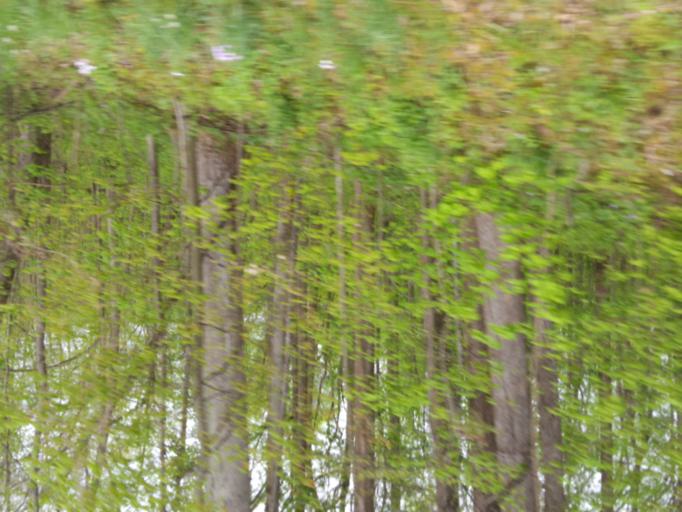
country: US
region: Ohio
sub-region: Knox County
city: Fredericktown
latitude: 40.5501
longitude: -82.5464
